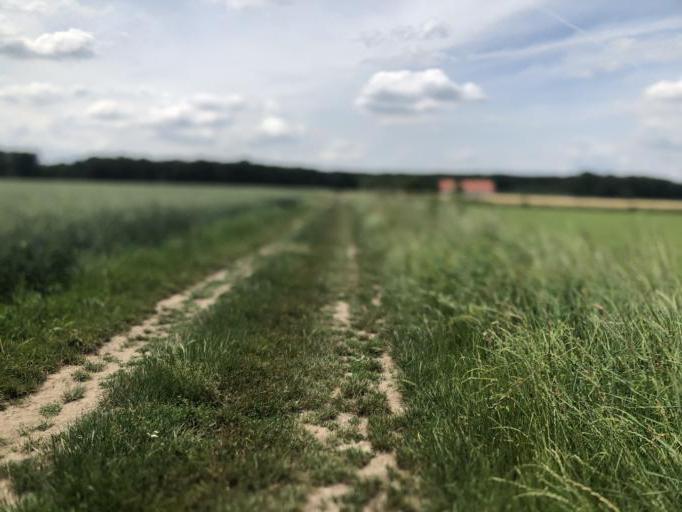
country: DE
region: Bavaria
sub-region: Regierungsbezirk Mittelfranken
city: Obermichelbach
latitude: 49.5761
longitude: 10.9409
